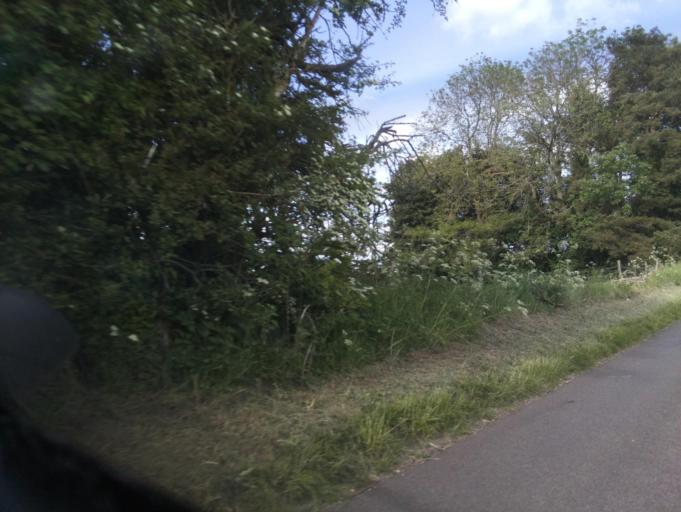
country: GB
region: England
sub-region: Gloucestershire
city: Shipton Village
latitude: 51.8740
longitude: -1.9203
